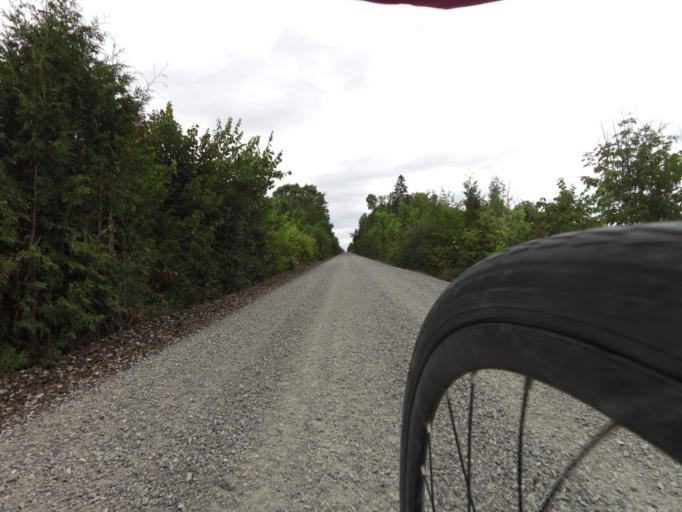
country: CA
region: Ontario
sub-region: Lanark County
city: Smiths Falls
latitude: 44.9884
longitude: -76.0618
